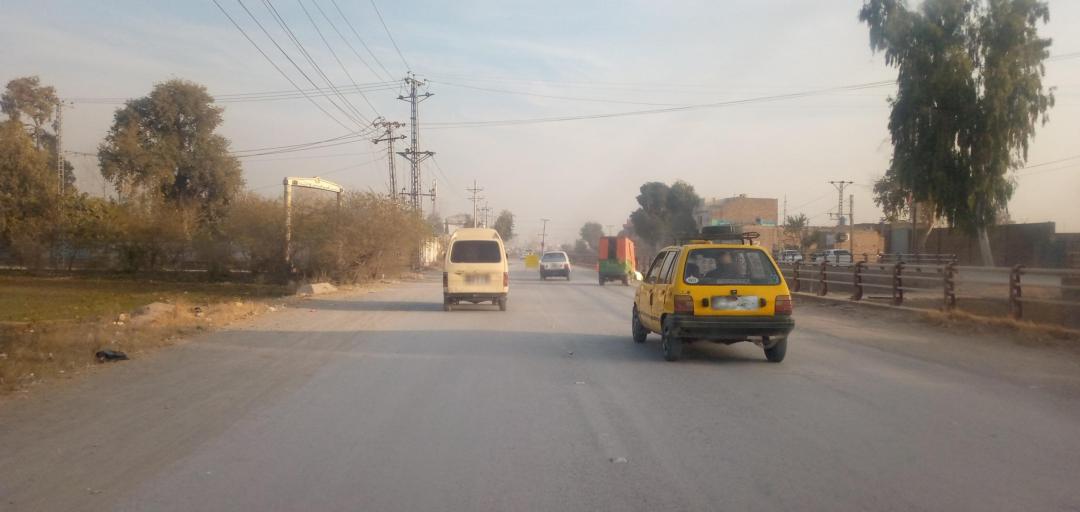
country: PK
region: Khyber Pakhtunkhwa
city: Peshawar
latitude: 33.9708
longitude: 71.5347
